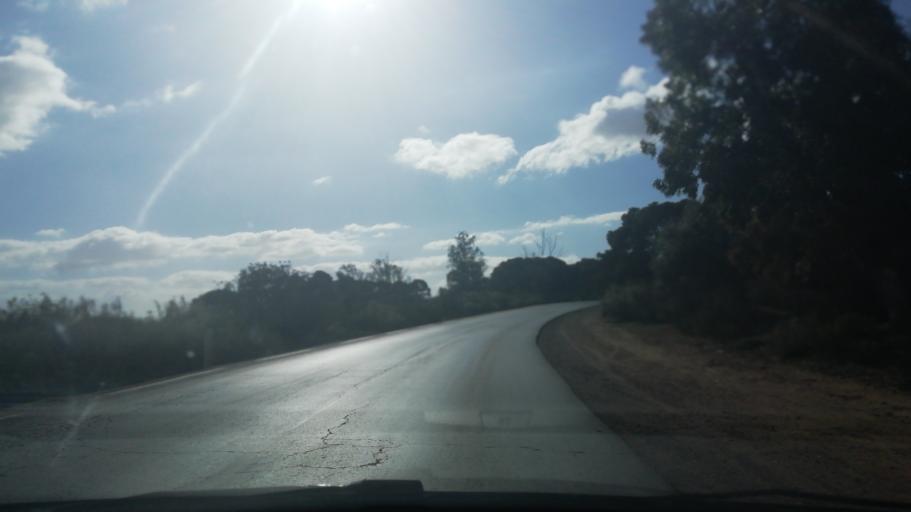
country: DZ
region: Mostaganem
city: Mostaganem
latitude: 35.9554
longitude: 0.2445
